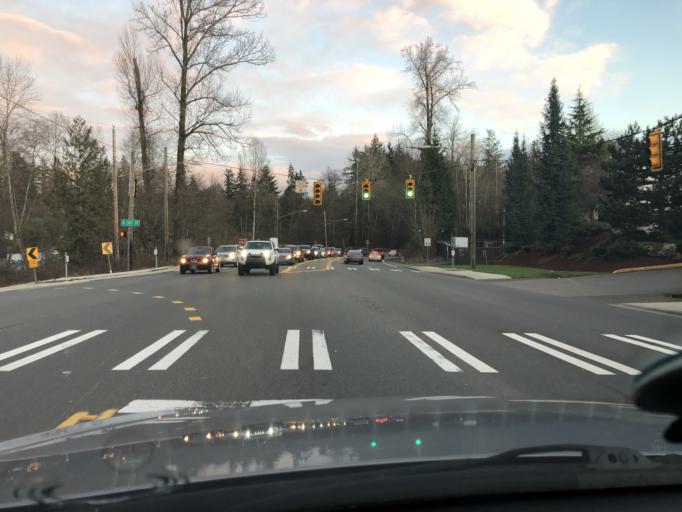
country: US
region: Washington
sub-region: King County
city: Lakeland North
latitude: 47.3142
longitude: -122.2811
